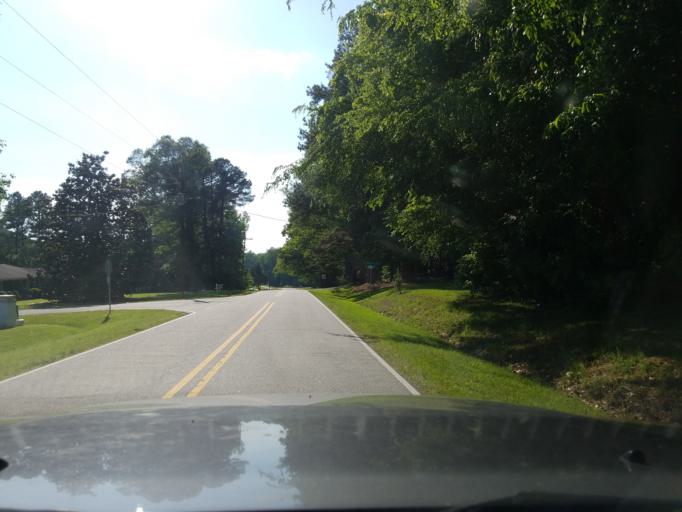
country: US
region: North Carolina
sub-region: Vance County
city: Henderson
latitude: 36.4078
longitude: -78.3762
